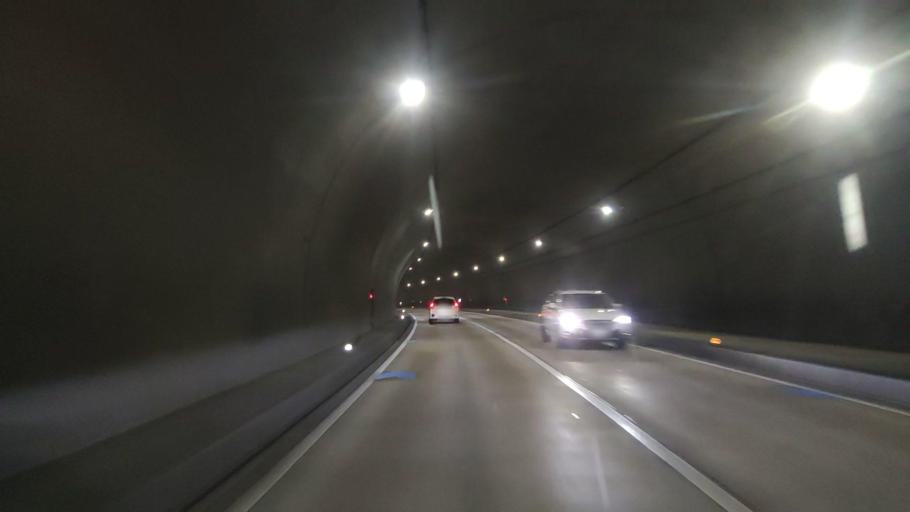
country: JP
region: Wakayama
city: Shingu
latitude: 33.7392
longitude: 135.9907
